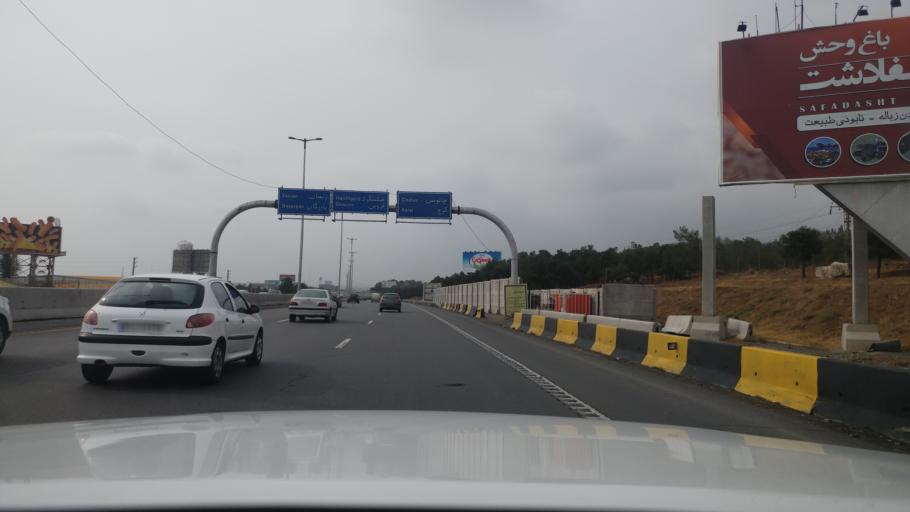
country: IR
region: Tehran
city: Shahr-e Qods
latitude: 35.7176
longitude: 51.2331
